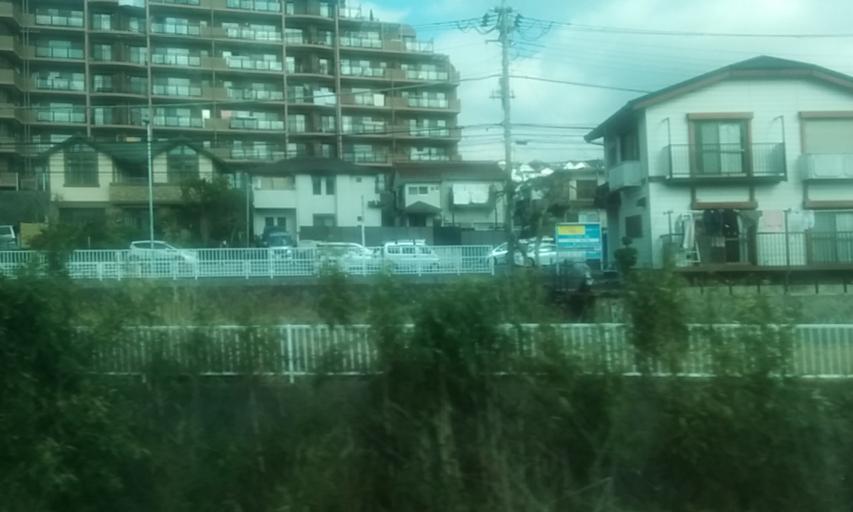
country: JP
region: Kanagawa
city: Yokohama
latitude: 35.4441
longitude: 139.5716
